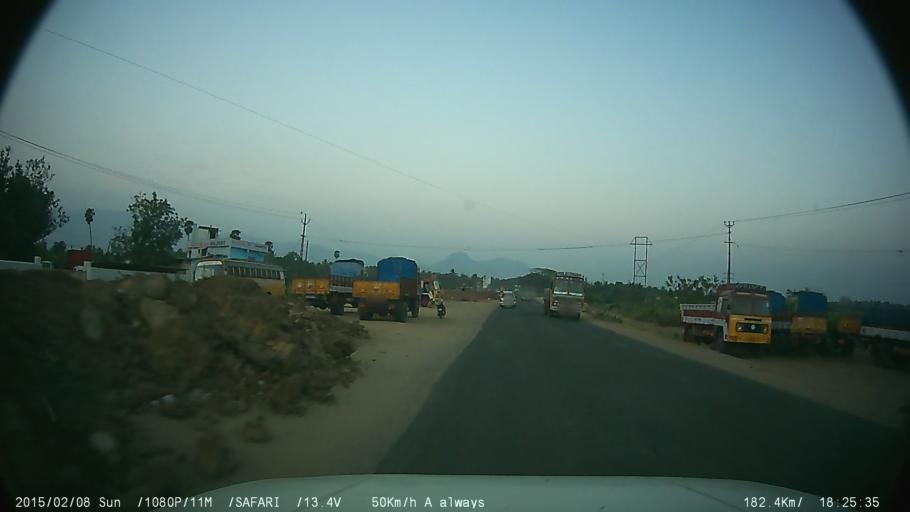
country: IN
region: Kerala
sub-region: Palakkad district
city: Palakkad
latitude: 10.7630
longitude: 76.6741
